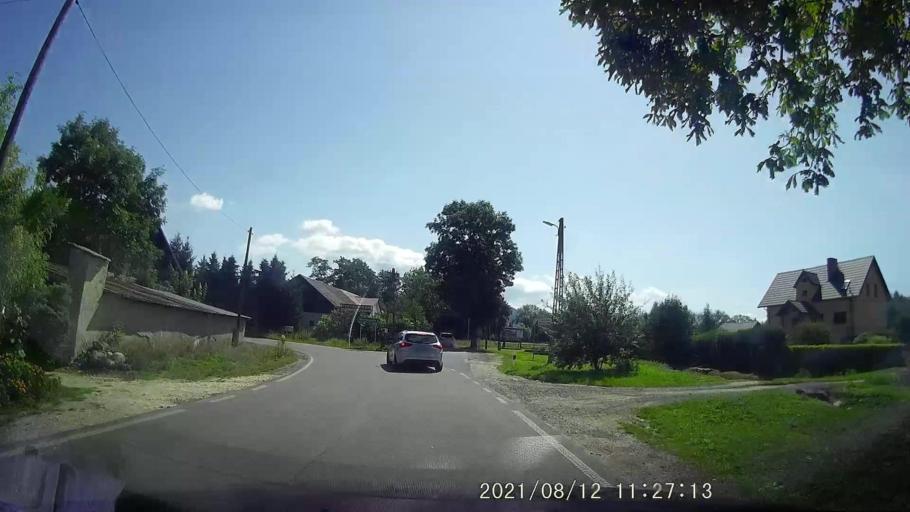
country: PL
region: Lower Silesian Voivodeship
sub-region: Powiat klodzki
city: Bystrzyca Klodzka
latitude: 50.2713
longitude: 16.6936
